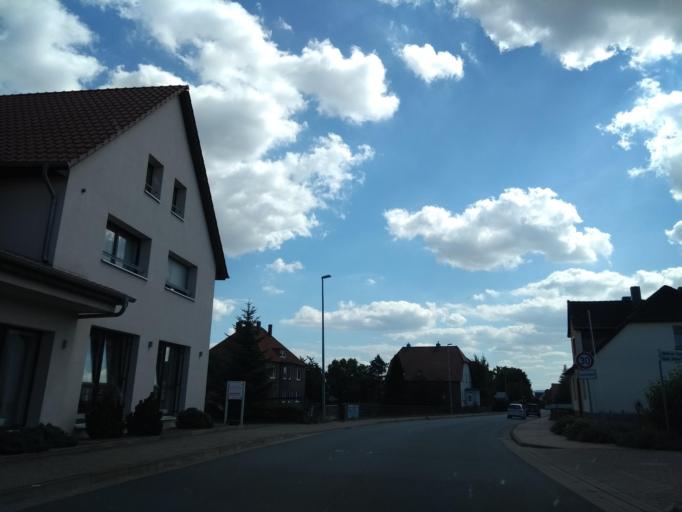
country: DE
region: Lower Saxony
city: Wunstorf
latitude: 52.4475
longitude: 9.4205
